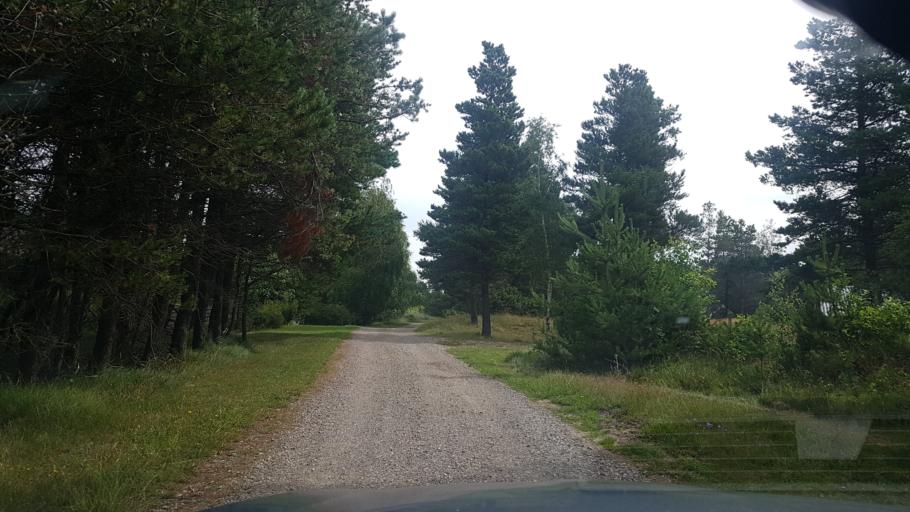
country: DE
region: Schleswig-Holstein
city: List
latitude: 55.0902
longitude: 8.5253
